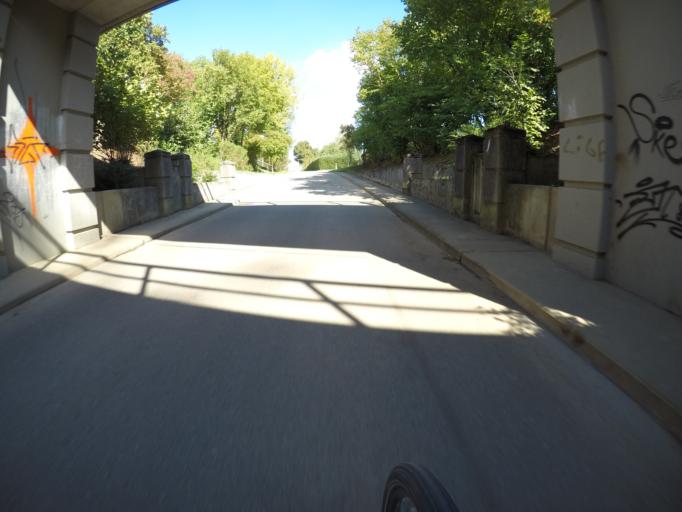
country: DE
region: Baden-Wuerttemberg
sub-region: Regierungsbezirk Stuttgart
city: Leinfelden-Echterdingen
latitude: 48.7164
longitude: 9.1417
